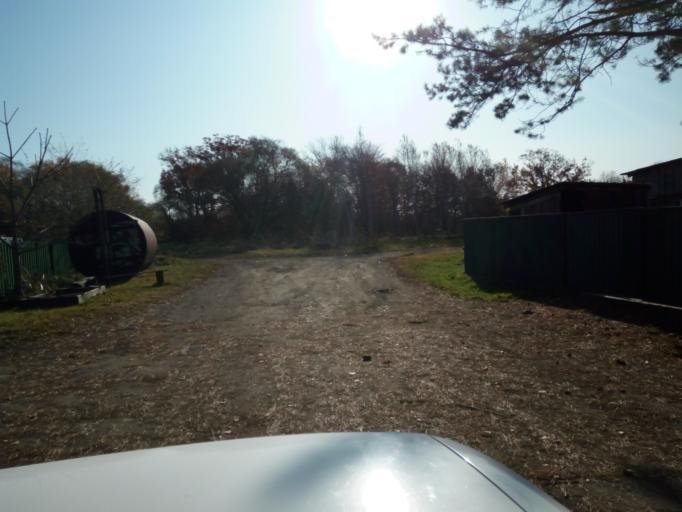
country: RU
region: Primorskiy
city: Lazo
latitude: 45.8663
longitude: 133.6506
